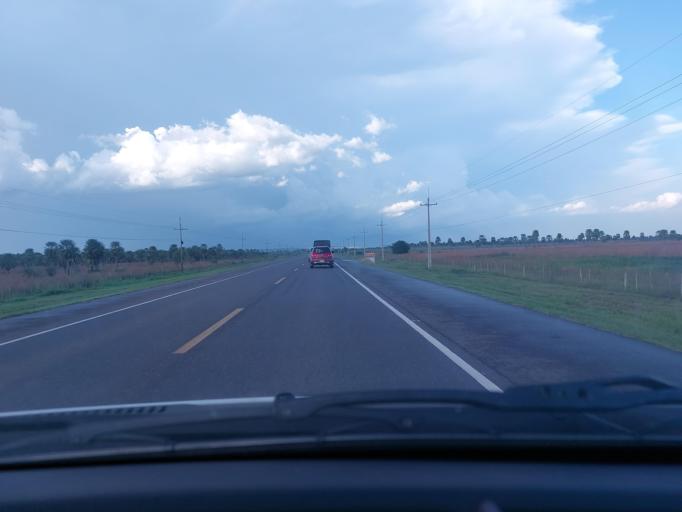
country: PY
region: Cordillera
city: Emboscada
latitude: -25.0804
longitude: -57.2750
